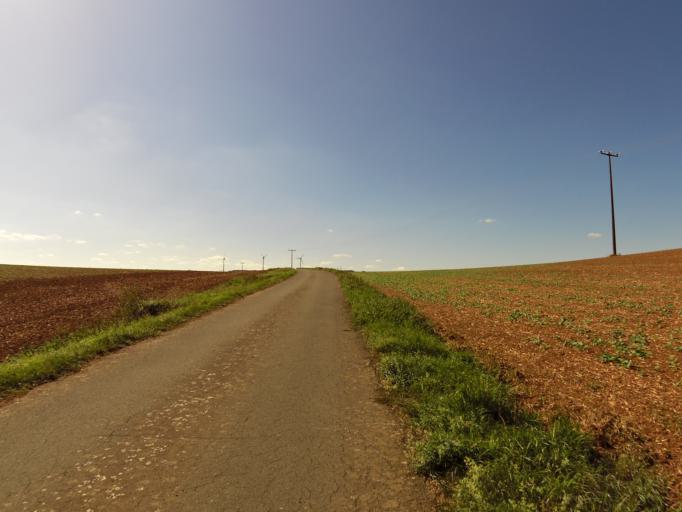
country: DE
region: Rheinland-Pfalz
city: Borrstadt
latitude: 49.5802
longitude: 7.9622
